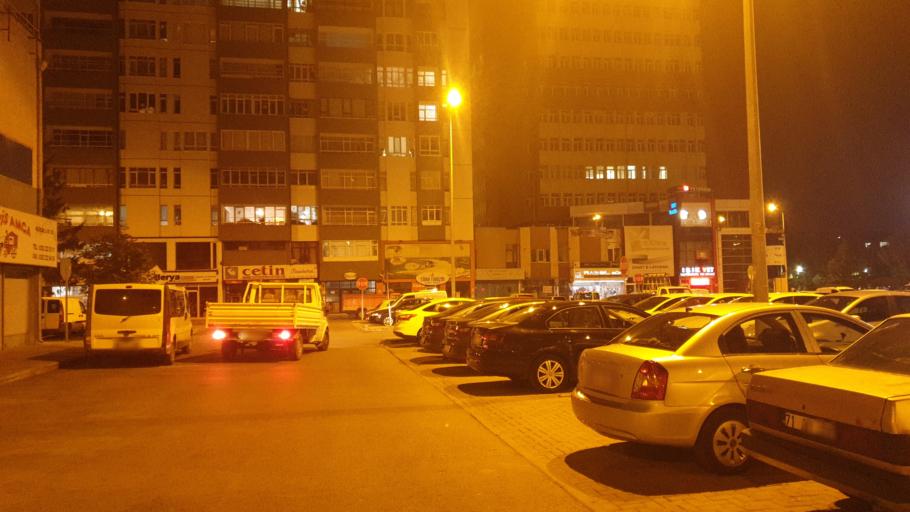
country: TR
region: Kayseri
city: Kayseri
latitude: 38.7287
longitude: 35.4951
